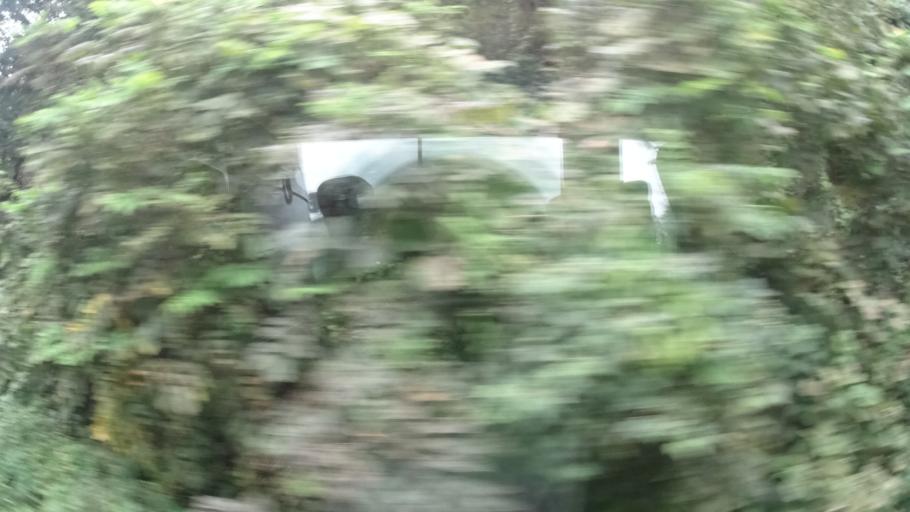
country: JP
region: Niigata
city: Murakami
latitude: 38.4445
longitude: 139.4855
